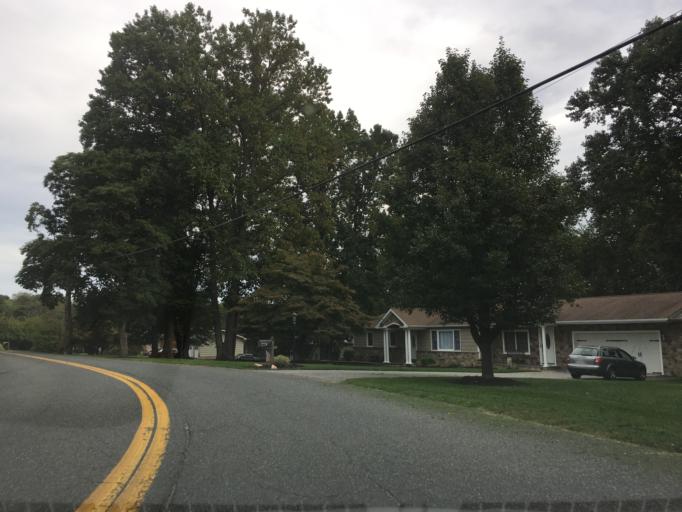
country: US
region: Maryland
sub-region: Baltimore County
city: Hunt Valley
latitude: 39.5061
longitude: -76.5809
